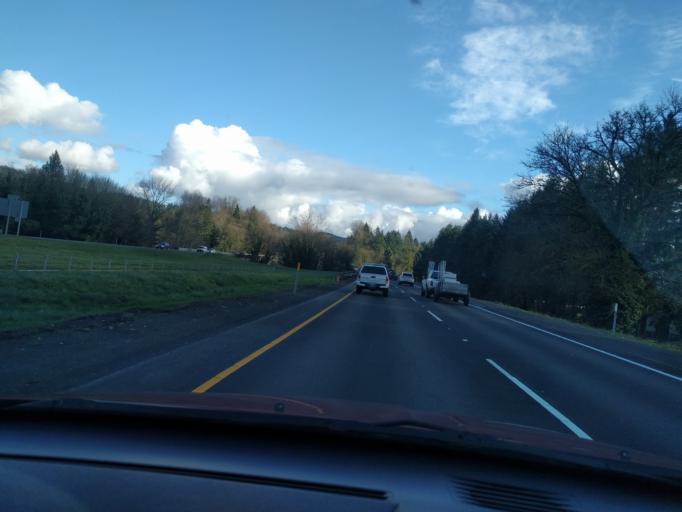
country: US
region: Oregon
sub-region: Clackamas County
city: Stafford
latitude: 45.3668
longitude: -122.6923
